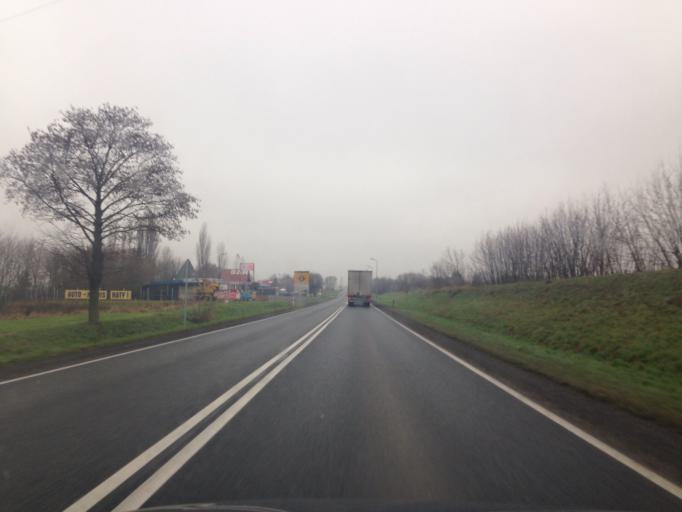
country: PL
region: Kujawsko-Pomorskie
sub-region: Powiat nakielski
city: Naklo nad Notecia
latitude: 53.1567
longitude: 17.6231
